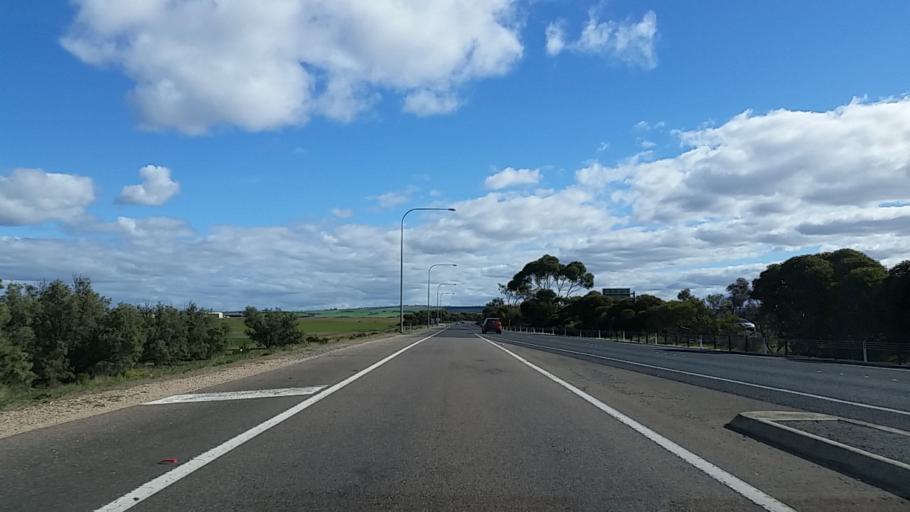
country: AU
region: South Australia
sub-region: Murray Bridge
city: Murray Bridge
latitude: -35.1515
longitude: 139.2827
